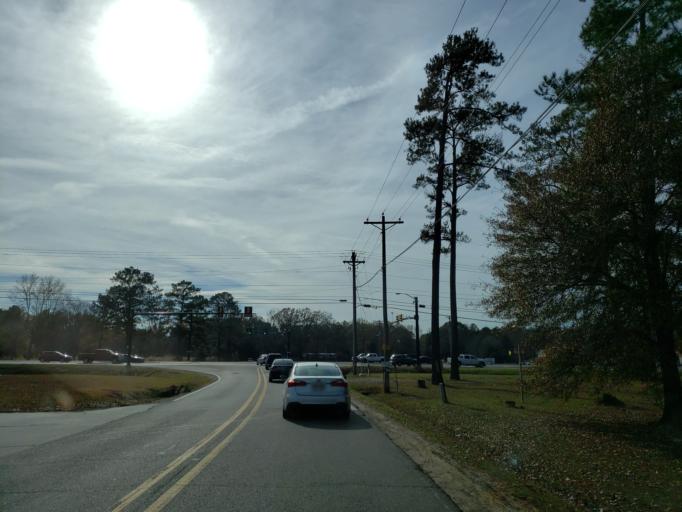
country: US
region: Mississippi
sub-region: Forrest County
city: Rawls Springs
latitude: 31.3910
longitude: -89.3771
